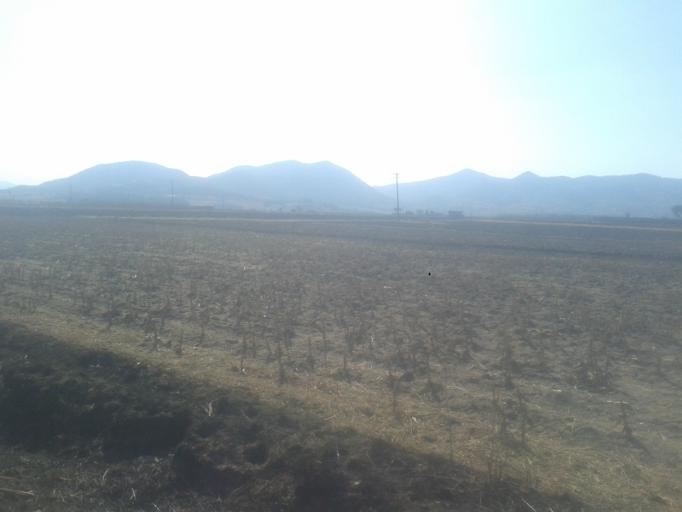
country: MX
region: Mexico
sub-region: Atlacomulco
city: San Bartolo Lanzados
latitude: 19.9026
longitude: -99.8626
